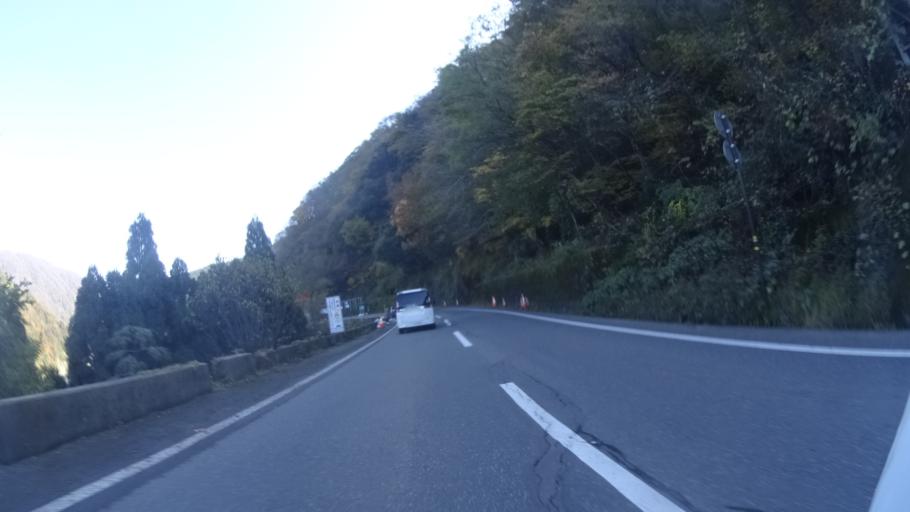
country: JP
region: Fukui
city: Ono
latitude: 35.9680
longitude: 136.5759
